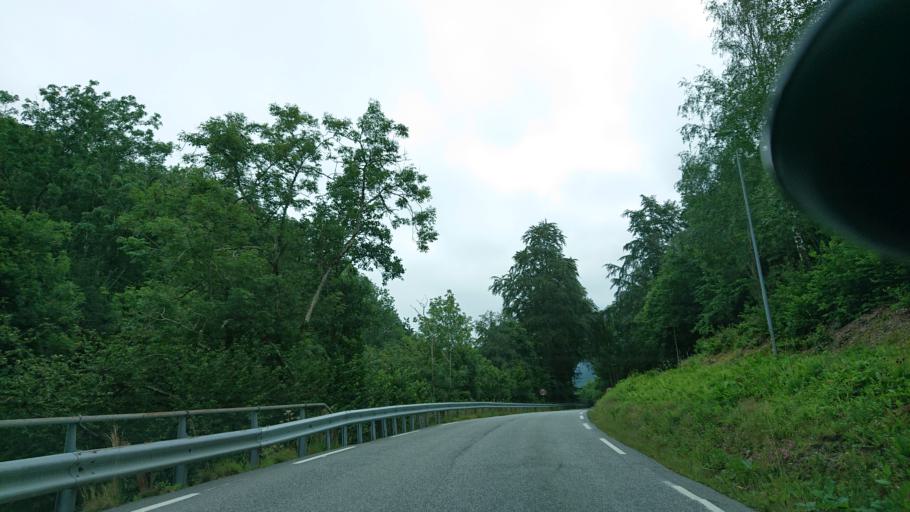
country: NO
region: Rogaland
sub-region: Hjelmeland
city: Hjelmelandsvagen
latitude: 59.2360
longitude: 6.1821
